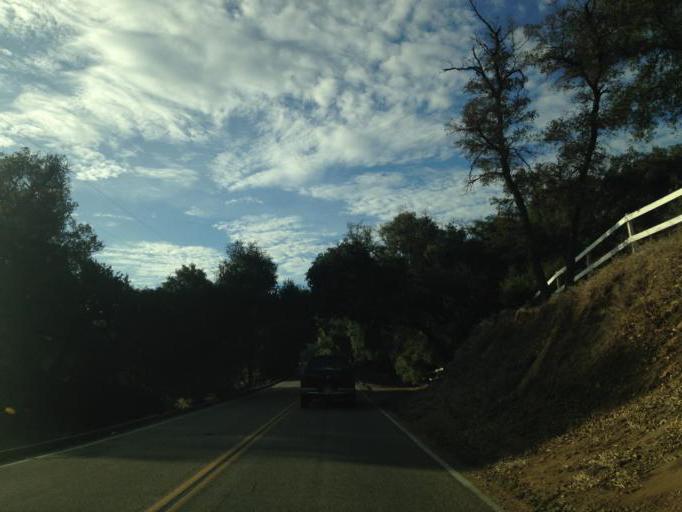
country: US
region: California
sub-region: San Diego County
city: Rainbow
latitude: 33.4367
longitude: -117.0896
